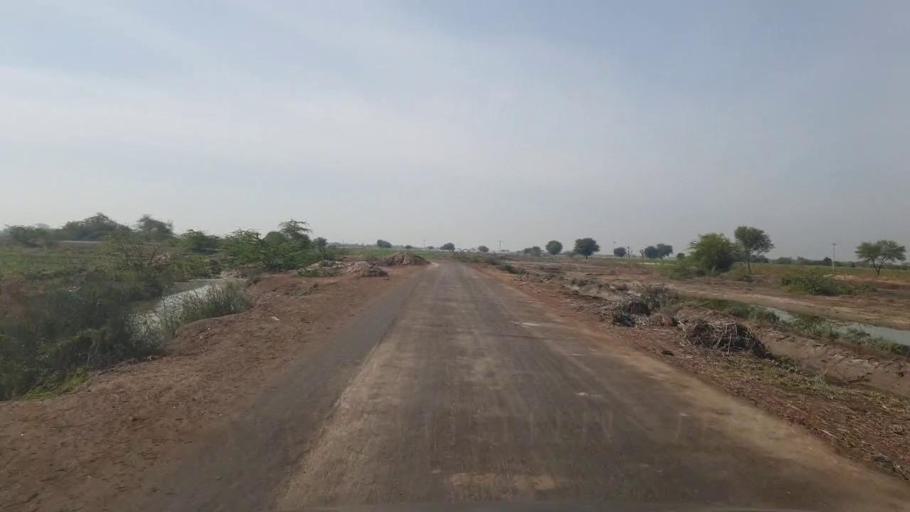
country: PK
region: Sindh
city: Umarkot
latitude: 25.3593
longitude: 69.6809
